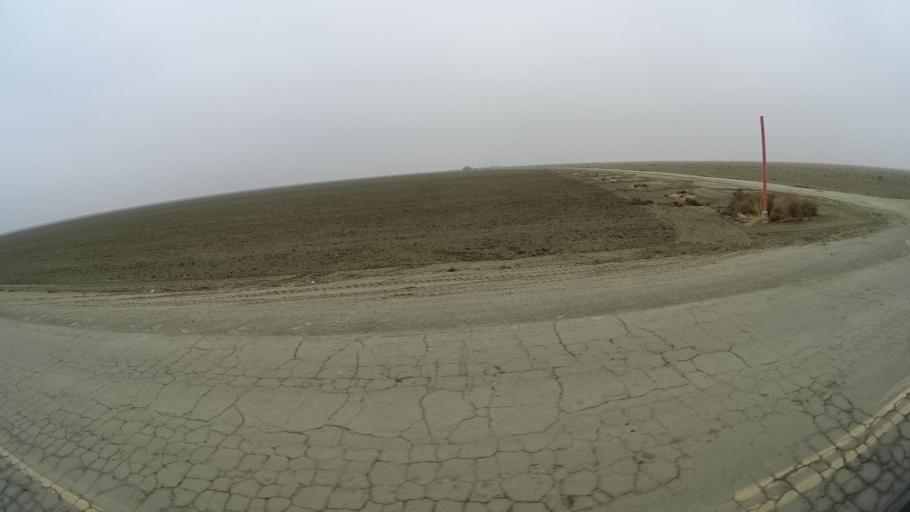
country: US
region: California
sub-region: Kern County
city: Maricopa
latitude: 35.1569
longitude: -119.1990
